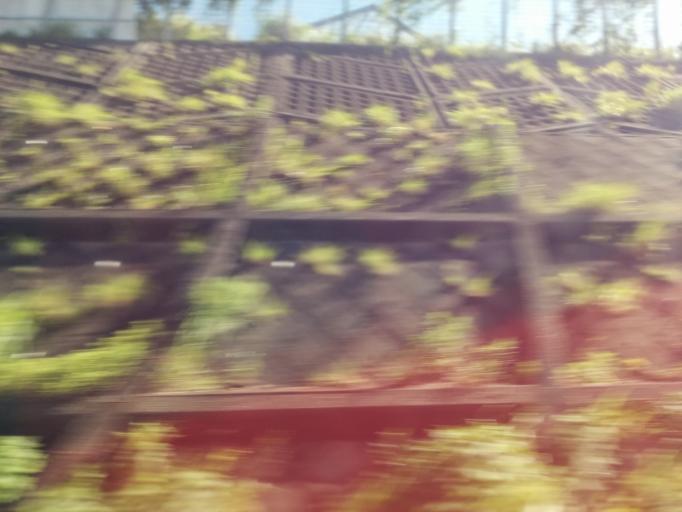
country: JP
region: Shizuoka
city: Numazu
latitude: 35.1409
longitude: 138.8124
